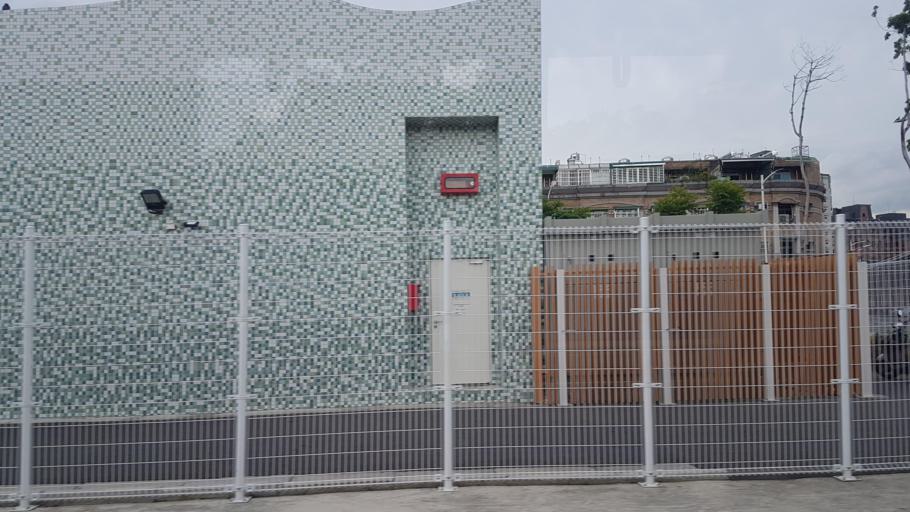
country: TW
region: Kaohsiung
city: Kaohsiung
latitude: 22.6451
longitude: 120.2812
